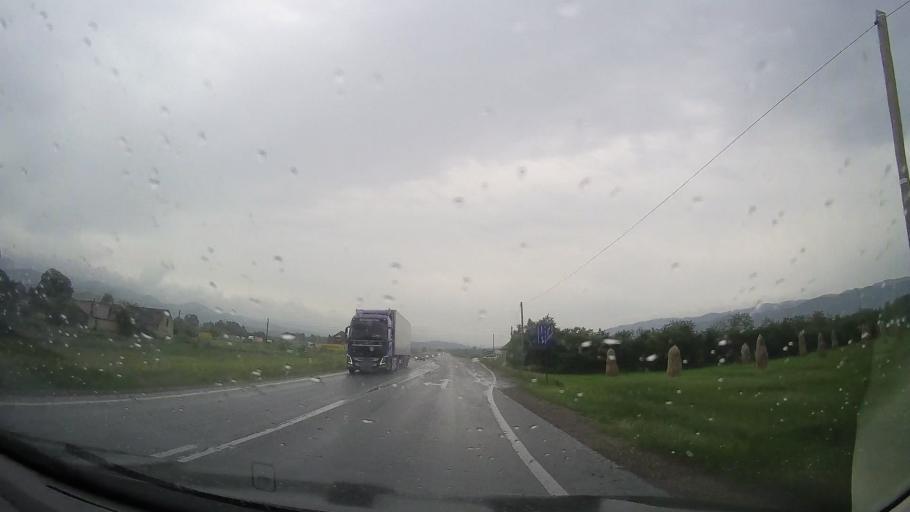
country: RO
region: Caras-Severin
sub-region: Comuna Bucosnita
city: Bucosnita
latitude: 45.3042
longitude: 22.2804
